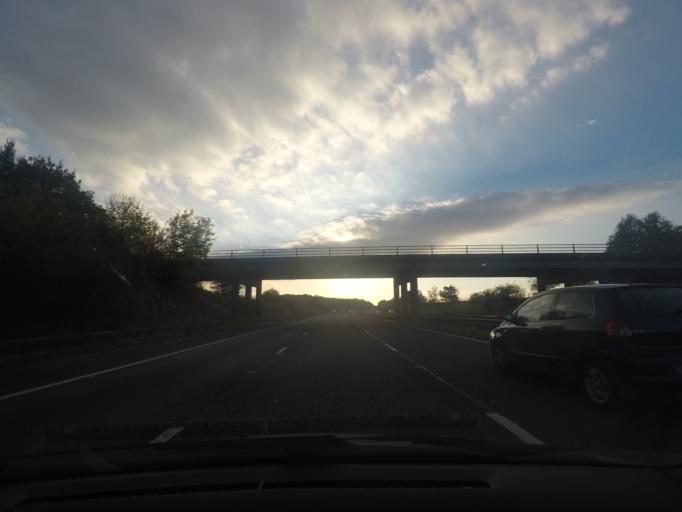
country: GB
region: England
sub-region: North Lincolnshire
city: Brigg
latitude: 53.5526
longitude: -0.5151
